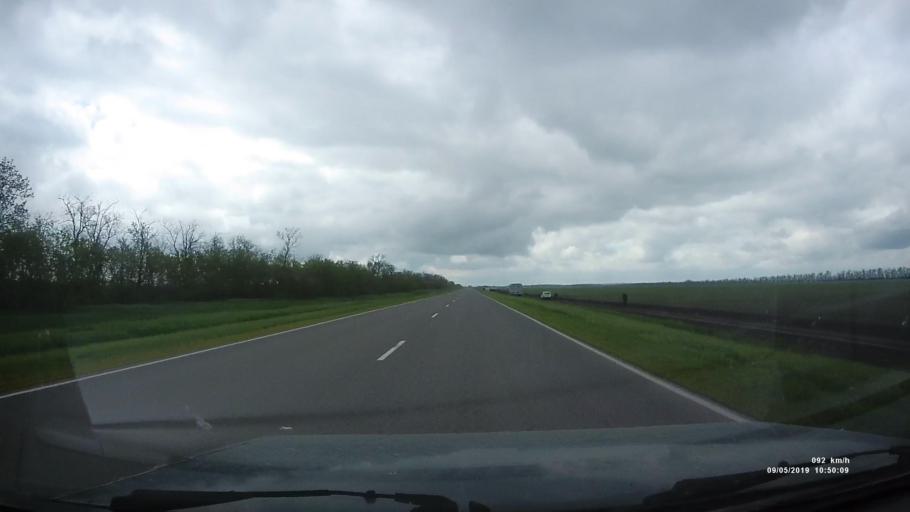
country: RU
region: Rostov
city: Peshkovo
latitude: 46.9326
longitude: 39.3554
